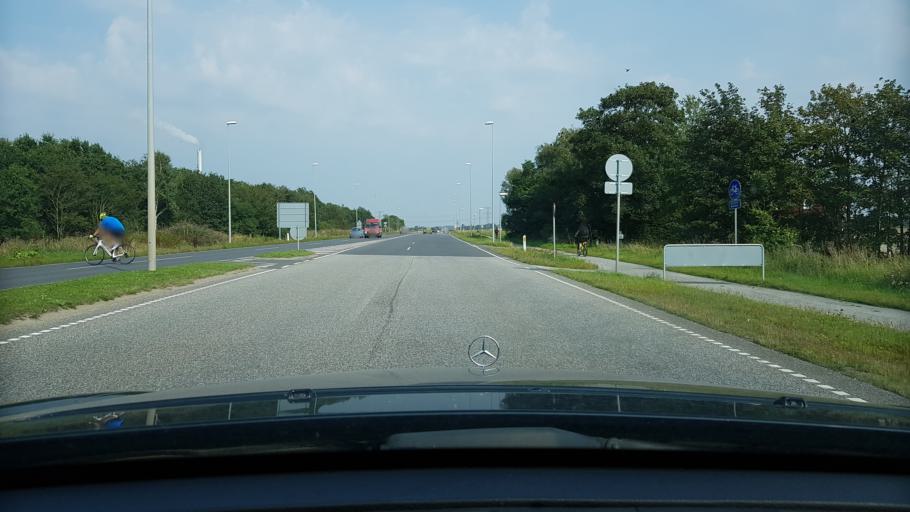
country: DK
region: North Denmark
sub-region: Alborg Kommune
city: Gistrup
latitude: 57.0205
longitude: 10.0065
